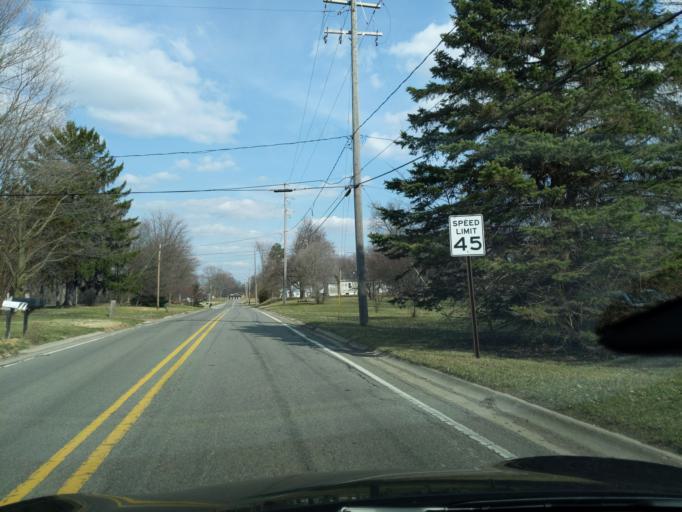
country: US
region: Michigan
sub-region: Jackson County
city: Jackson
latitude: 42.2736
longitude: -84.4203
